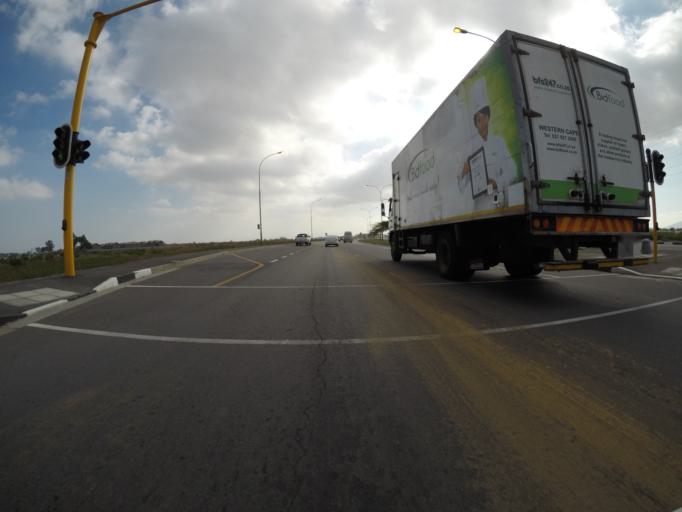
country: ZA
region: Western Cape
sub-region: City of Cape Town
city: Kraaifontein
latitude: -33.9560
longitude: 18.6871
